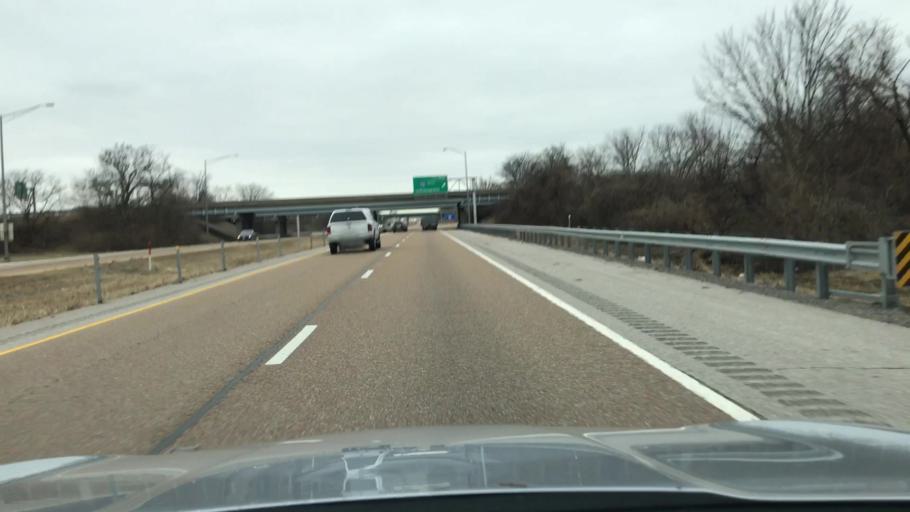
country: US
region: Illinois
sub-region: Madison County
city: Troy
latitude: 38.7538
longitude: -89.9069
